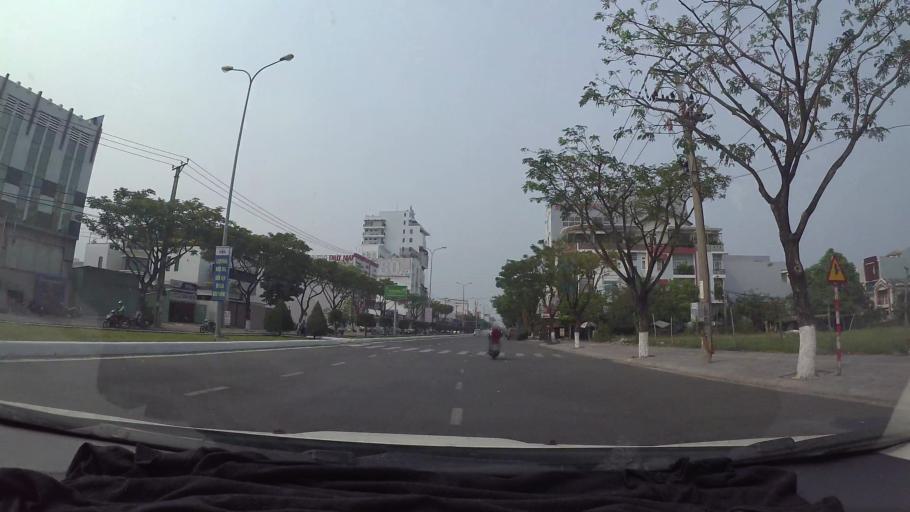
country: VN
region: Da Nang
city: Cam Le
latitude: 16.0403
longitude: 108.2107
